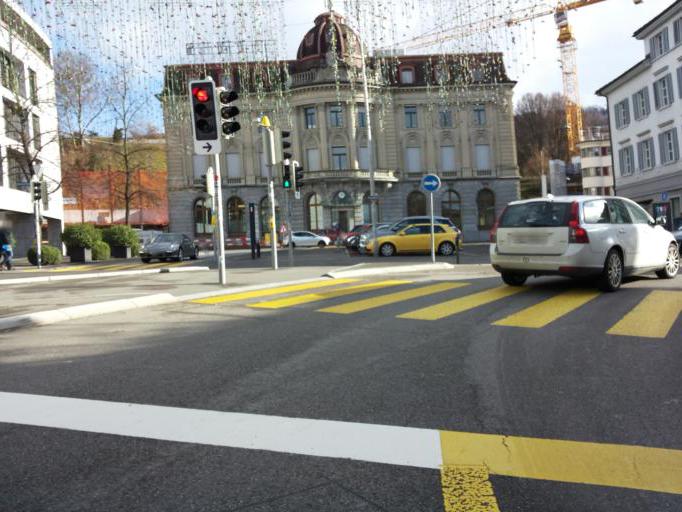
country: CH
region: Zug
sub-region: Zug
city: Zug
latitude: 47.1680
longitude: 8.5155
